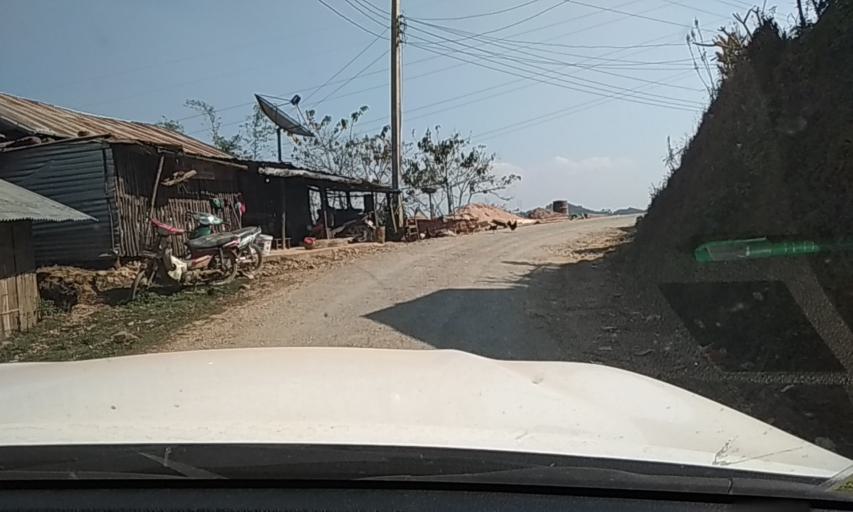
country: LA
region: Phongsali
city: Phongsali
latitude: 21.6602
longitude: 102.0915
